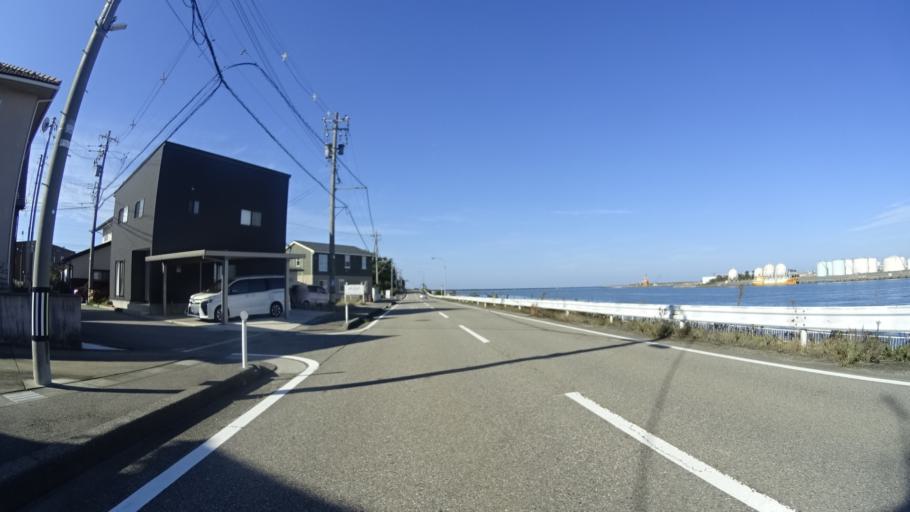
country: JP
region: Ishikawa
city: Kanazawa-shi
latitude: 36.6164
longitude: 136.6076
